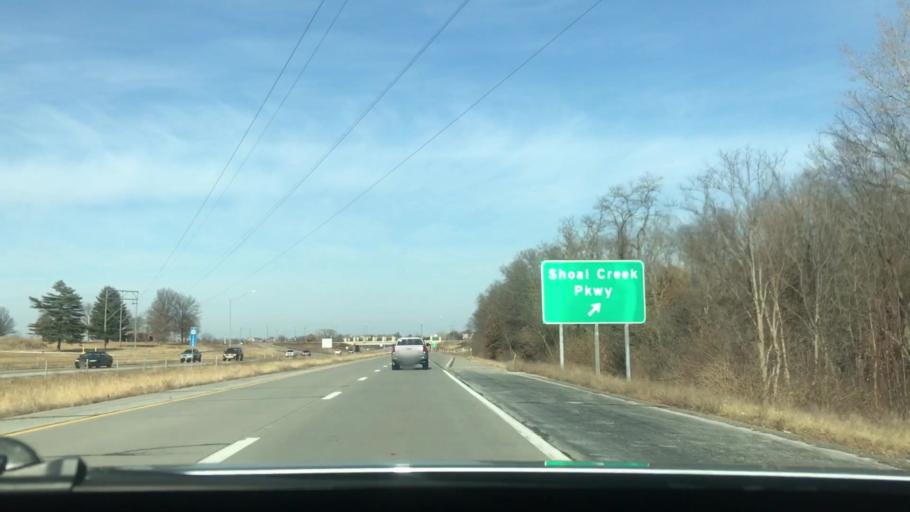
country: US
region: Missouri
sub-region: Clay County
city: Gladstone
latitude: 39.2840
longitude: -94.5850
